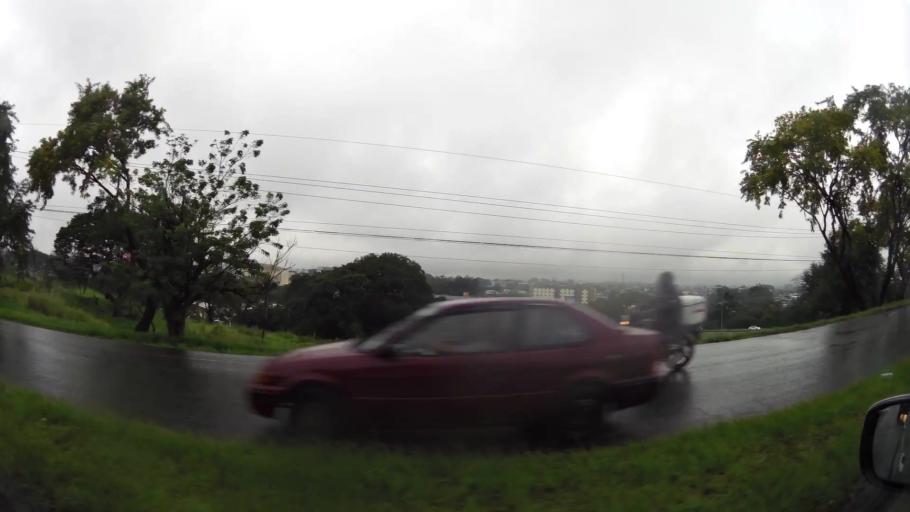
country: CR
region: Alajuela
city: Alajuela
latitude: 9.9995
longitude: -84.2070
